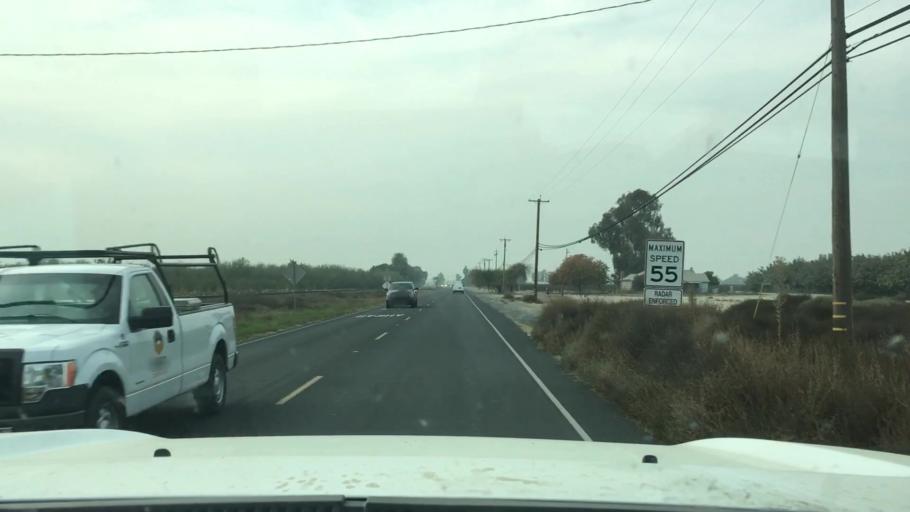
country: US
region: California
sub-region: San Joaquin County
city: Manteca
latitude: 37.8483
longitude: -121.1878
